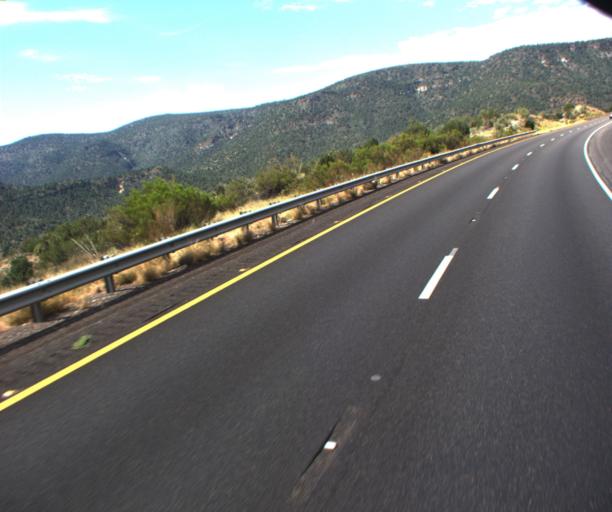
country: US
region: Arizona
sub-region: Yavapai County
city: Camp Verde
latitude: 34.5414
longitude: -111.9096
